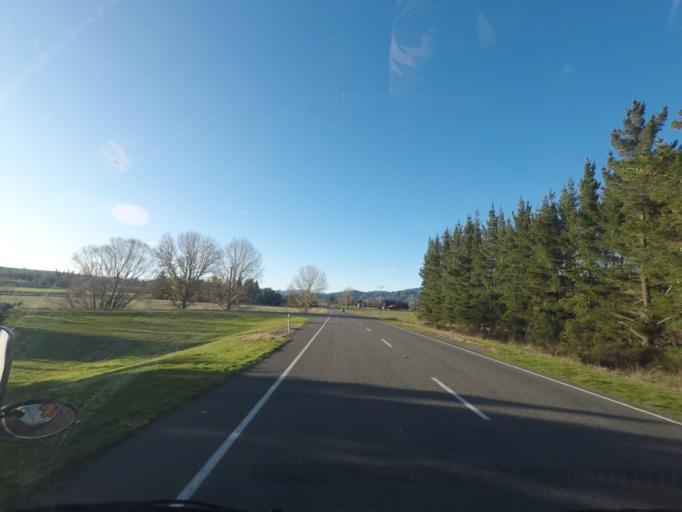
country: NZ
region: Canterbury
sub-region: Kaikoura District
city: Kaikoura
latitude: -42.7188
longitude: 173.2865
